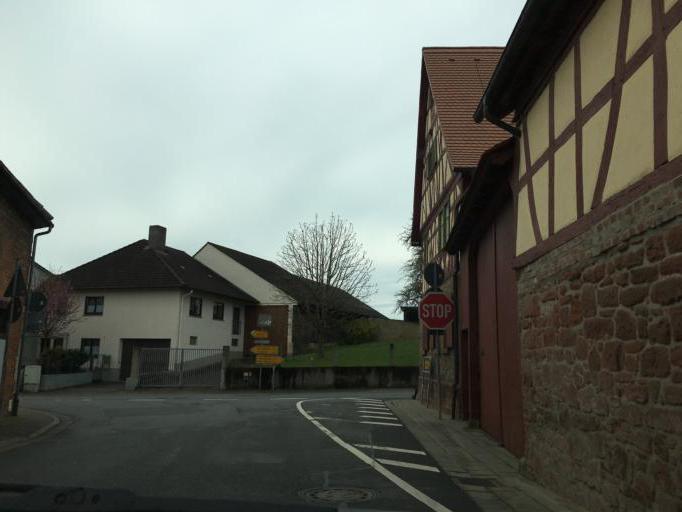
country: DE
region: Hesse
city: Reinheim
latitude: 49.8508
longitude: 8.8765
